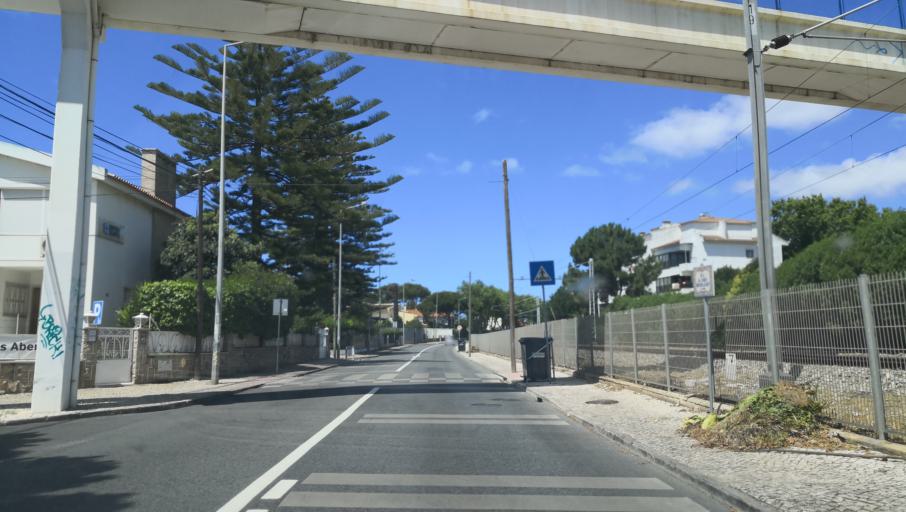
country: PT
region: Lisbon
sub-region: Cascais
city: Parede
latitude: 38.6874
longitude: -9.3475
